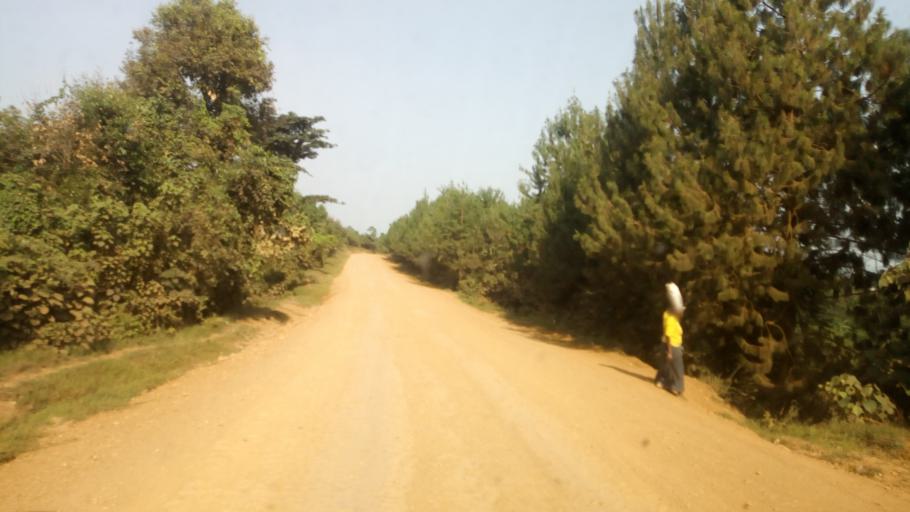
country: UG
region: Western Region
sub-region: Kanungu District
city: Ntungamo
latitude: -0.8273
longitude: 29.7046
